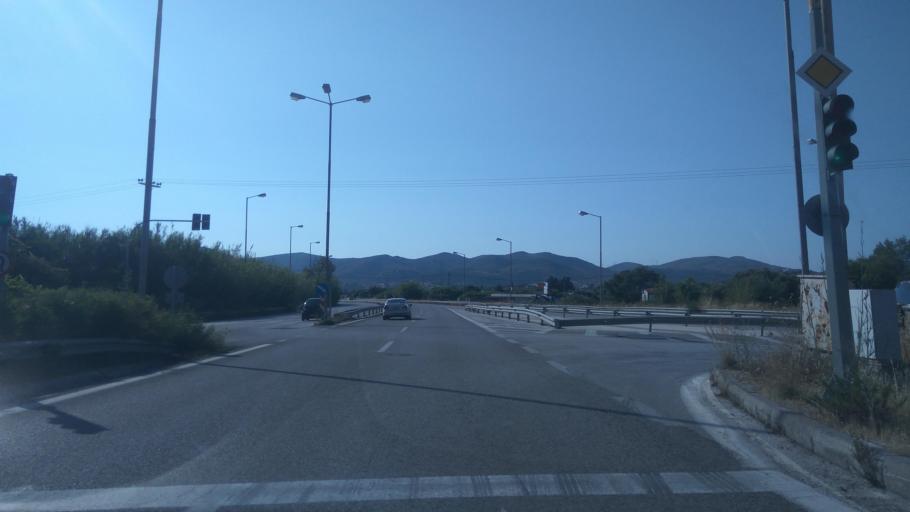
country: GR
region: Attica
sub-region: Nomarchia Anatolikis Attikis
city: Keratea
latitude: 37.8019
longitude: 23.9948
